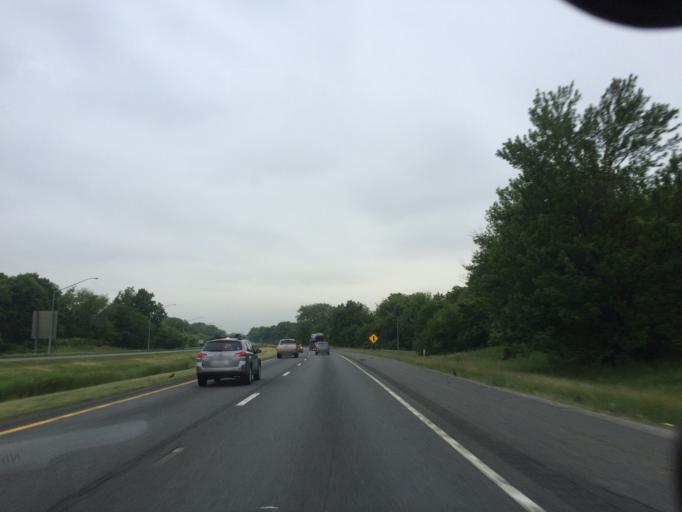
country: US
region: Maryland
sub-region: Washington County
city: Halfway
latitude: 39.6065
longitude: -77.7496
